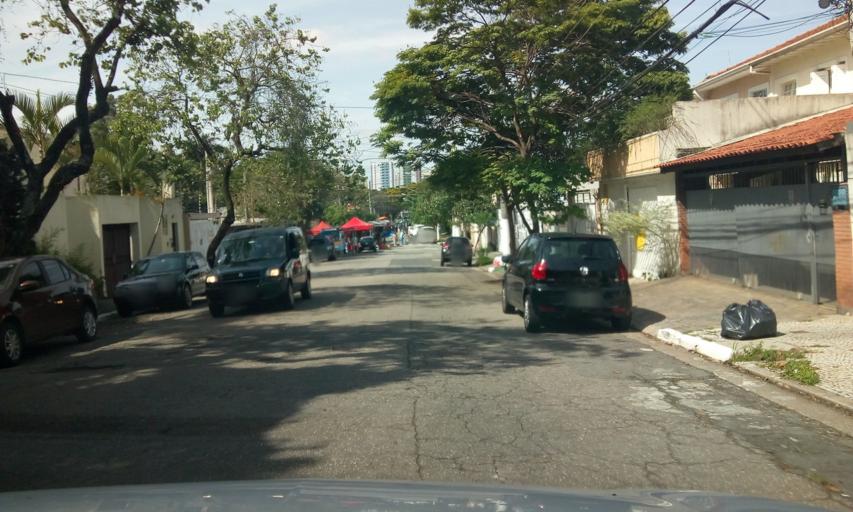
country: BR
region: Sao Paulo
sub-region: Sao Paulo
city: Sao Paulo
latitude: -23.6146
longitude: -46.6756
